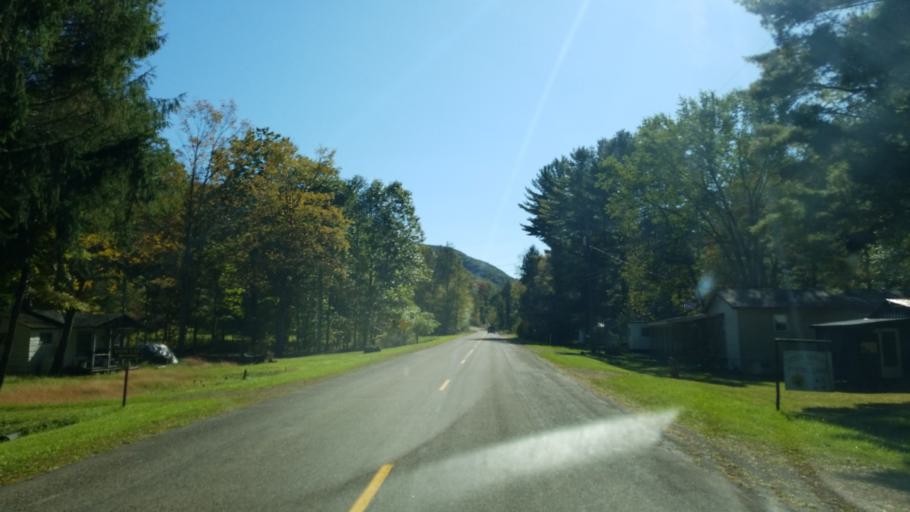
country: US
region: Pennsylvania
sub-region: Elk County
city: Saint Marys
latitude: 41.2725
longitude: -78.4021
